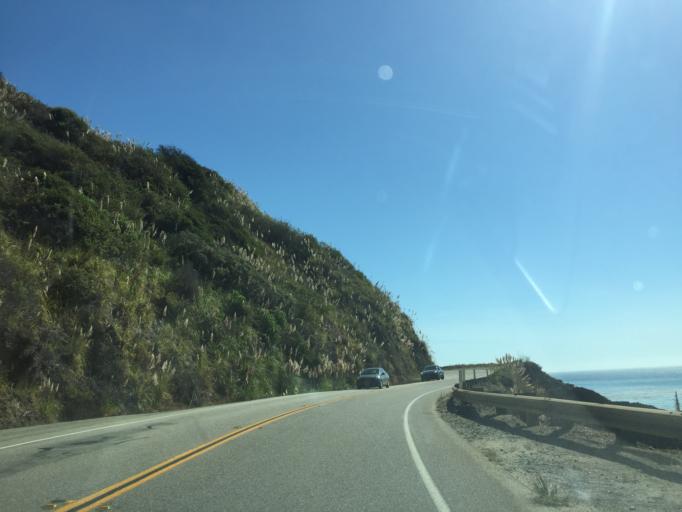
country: US
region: California
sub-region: Monterey County
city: Greenfield
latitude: 35.9812
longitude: -121.4901
